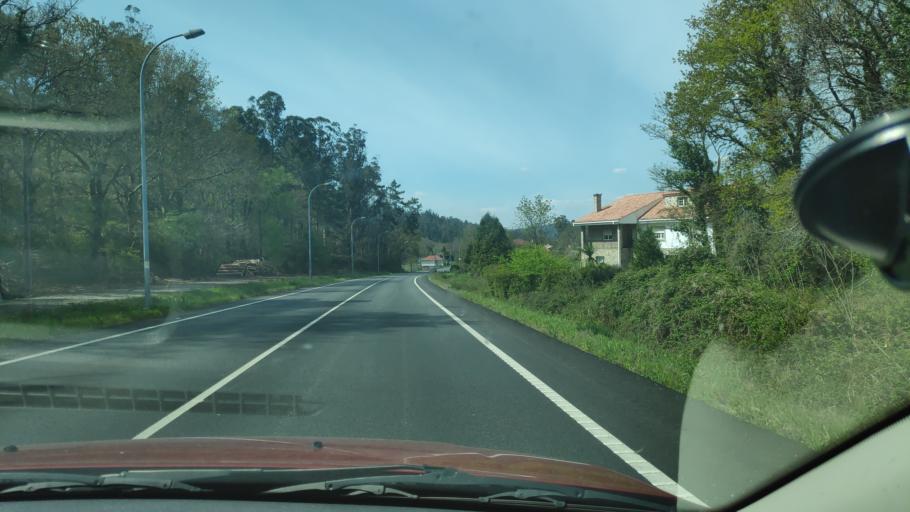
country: ES
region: Galicia
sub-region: Provincia da Coruna
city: Ames
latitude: 42.8815
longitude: -8.6800
